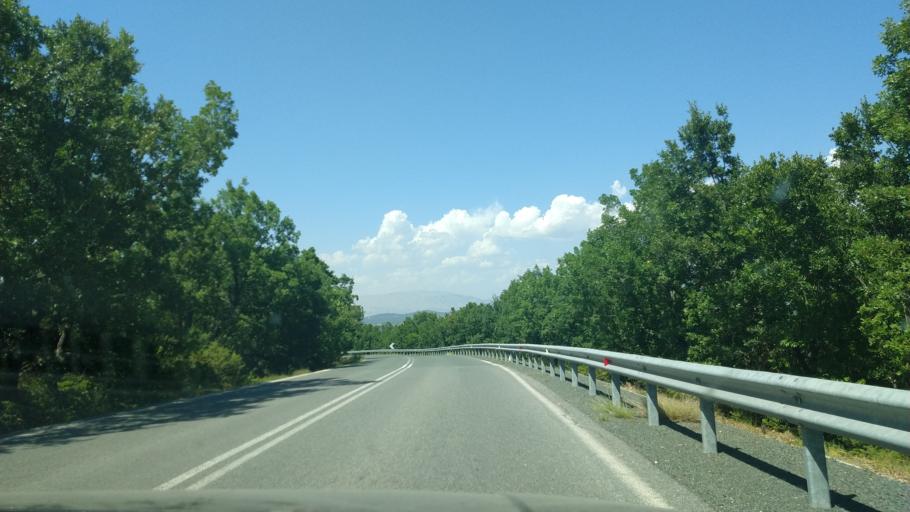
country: GR
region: West Macedonia
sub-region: Nomos Grevenon
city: Grevena
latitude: 40.0233
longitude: 21.4848
